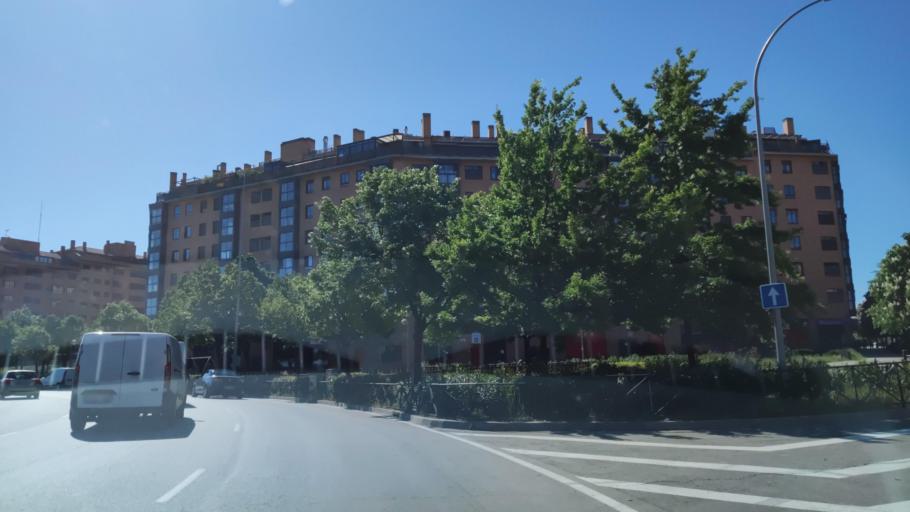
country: ES
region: Madrid
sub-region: Provincia de Madrid
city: San Blas
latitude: 40.4347
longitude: -3.6080
